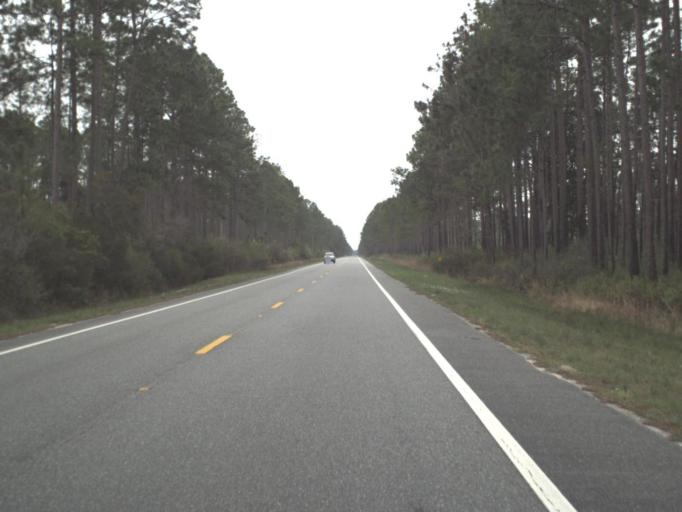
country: US
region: Florida
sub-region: Franklin County
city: Apalachicola
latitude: 29.8940
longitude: -84.9778
